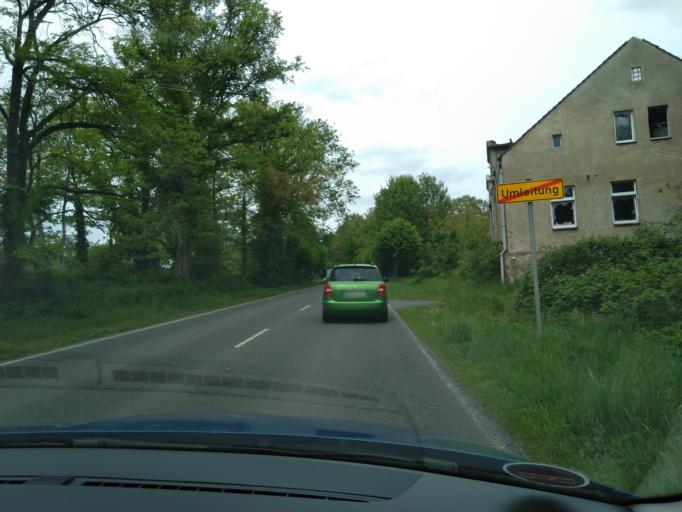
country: DE
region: Brandenburg
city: Oderberg
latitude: 52.8528
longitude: 14.0350
